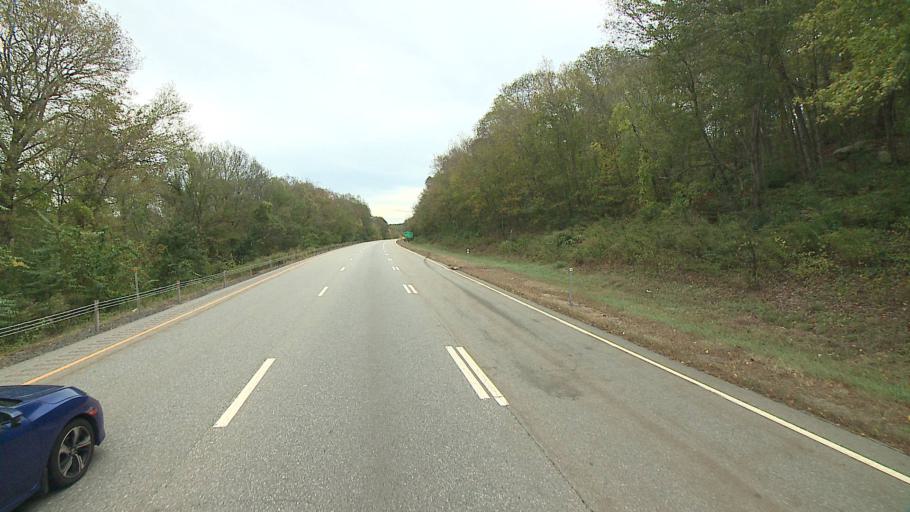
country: US
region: Connecticut
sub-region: Middlesex County
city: Deep River Center
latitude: 41.3764
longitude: -72.4396
